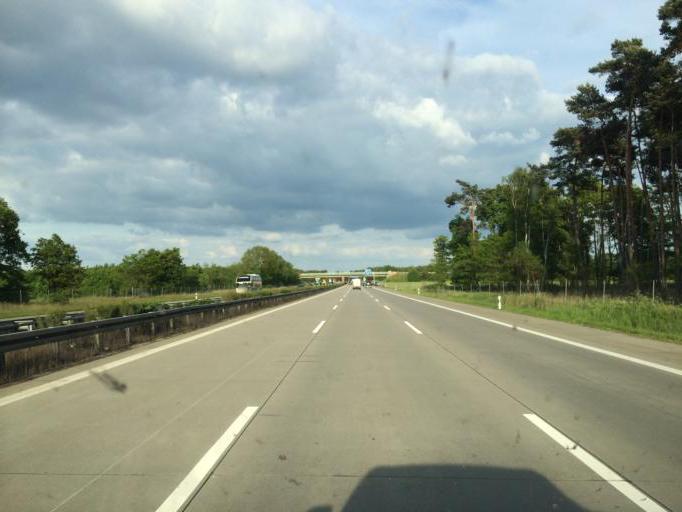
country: DE
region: Saxony-Anhalt
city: Loburg
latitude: 52.2332
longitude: 12.0393
